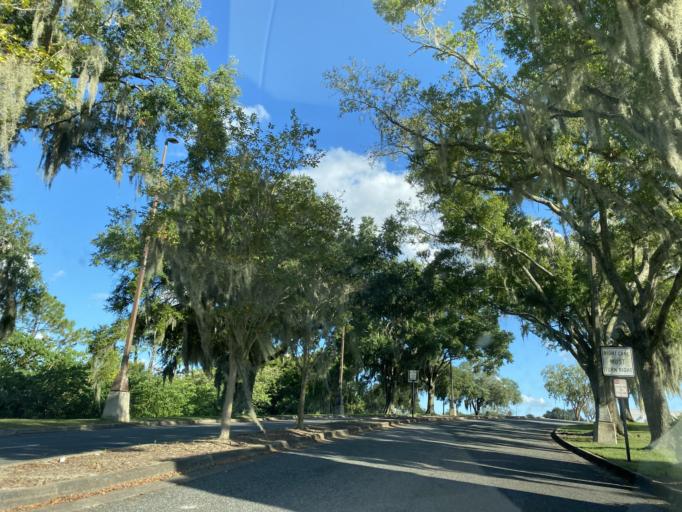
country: US
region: Florida
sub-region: Marion County
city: Ocala
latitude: 29.1616
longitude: -82.1732
